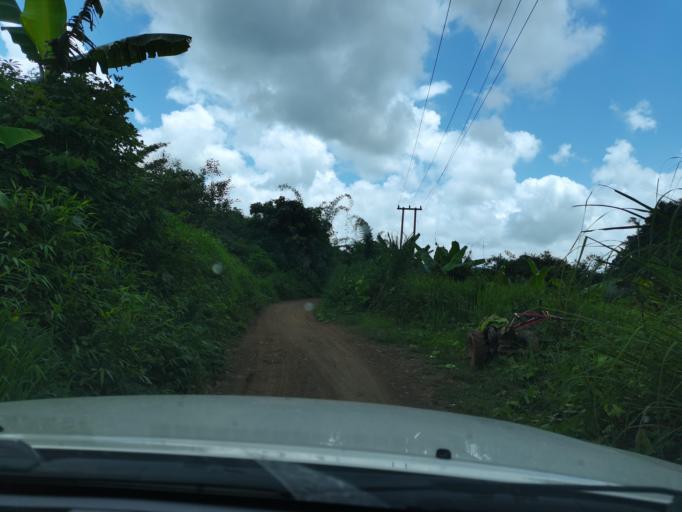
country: LA
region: Loungnamtha
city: Muang Long
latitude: 20.7589
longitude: 101.0167
